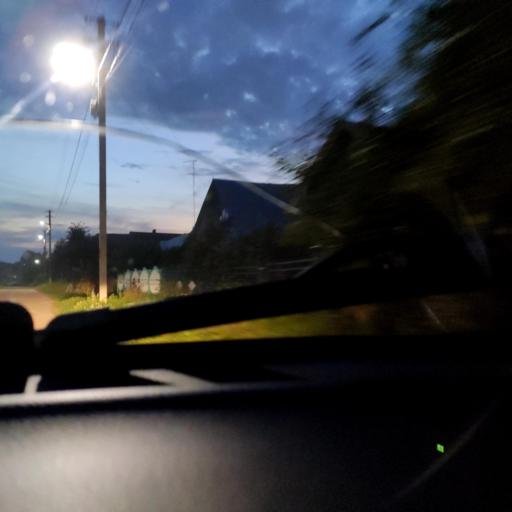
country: RU
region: Tatarstan
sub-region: Gorod Kazan'
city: Kazan
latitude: 55.8608
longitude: 49.0643
